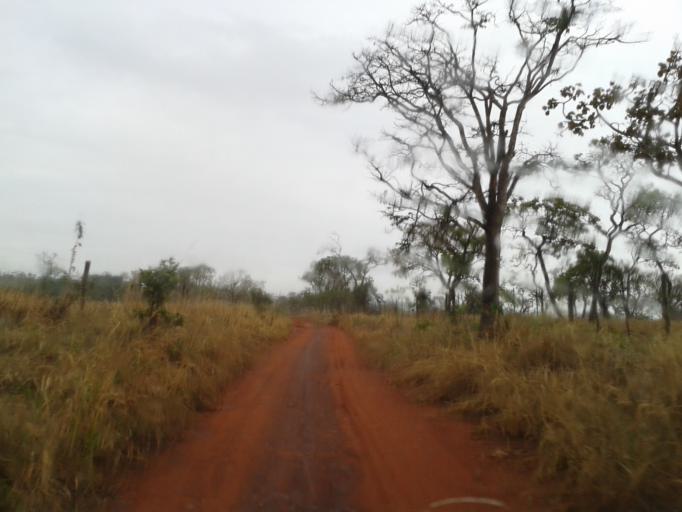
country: BR
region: Minas Gerais
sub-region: Campina Verde
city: Campina Verde
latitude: -19.3548
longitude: -49.5402
